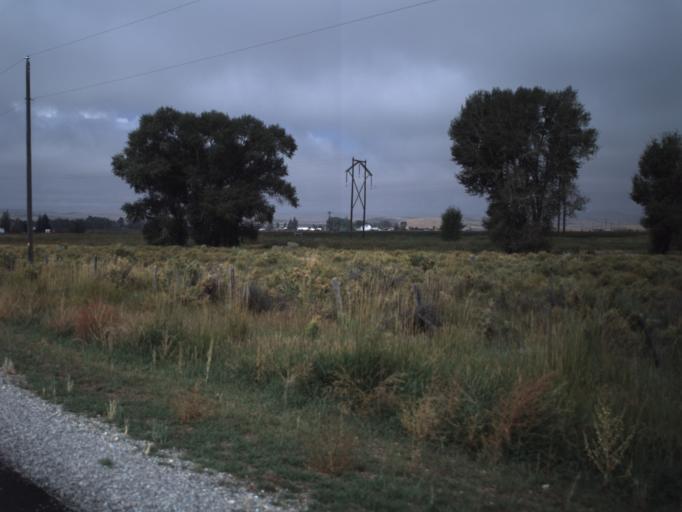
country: US
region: Utah
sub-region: Rich County
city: Randolph
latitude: 41.5174
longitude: -111.1459
